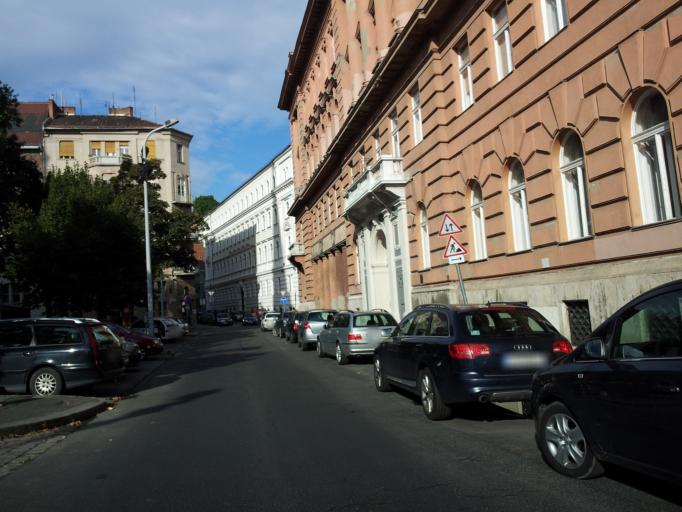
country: HU
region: Budapest
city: Budapest
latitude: 47.5042
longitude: 19.0392
